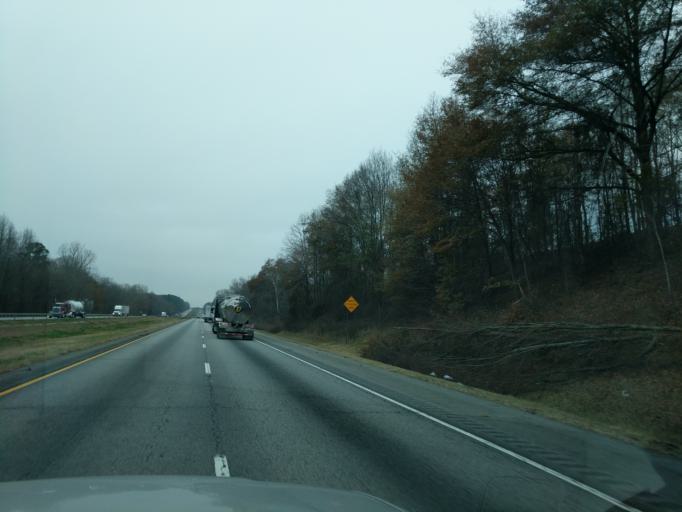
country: US
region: Georgia
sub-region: Franklin County
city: Carnesville
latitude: 34.3727
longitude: -83.2659
